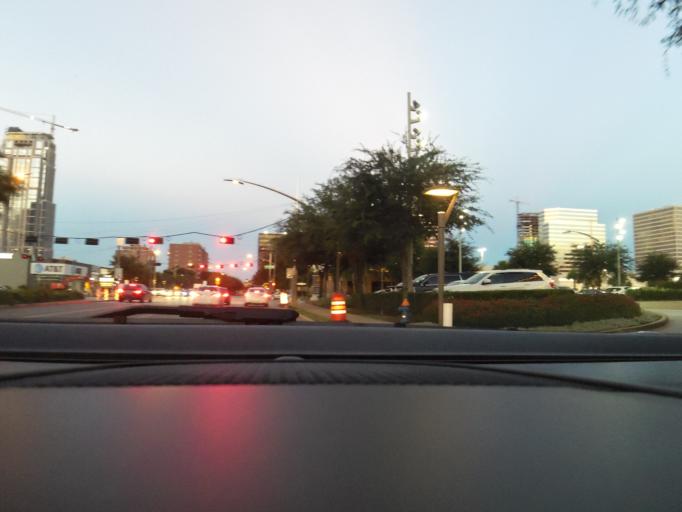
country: US
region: Texas
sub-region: Harris County
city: Hunters Creek Village
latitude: 29.7502
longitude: -95.4621
